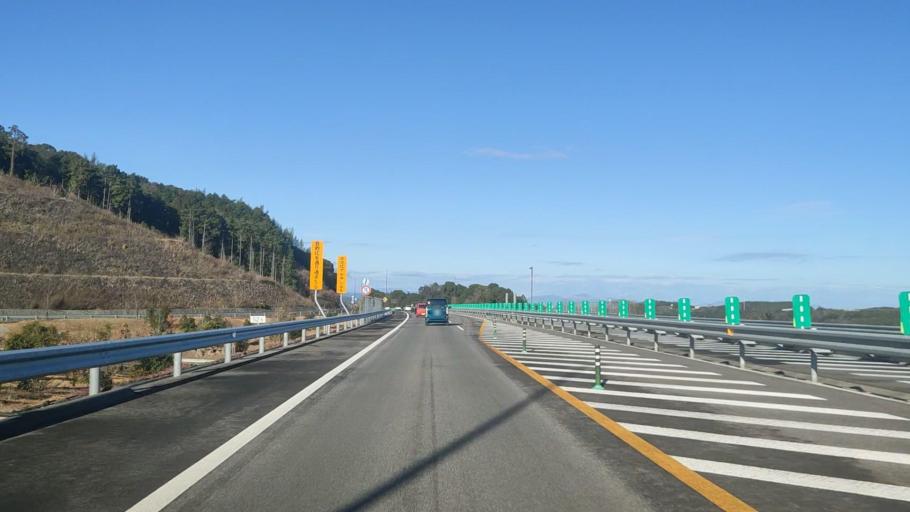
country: JP
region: Fukuoka
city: Nakatsu
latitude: 33.5321
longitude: 131.2344
